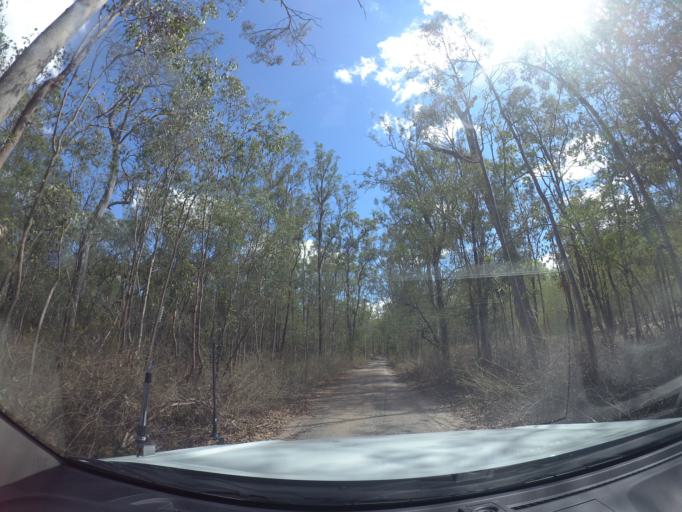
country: AU
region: Queensland
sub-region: Logan
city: North Maclean
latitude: -27.8224
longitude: 152.9691
